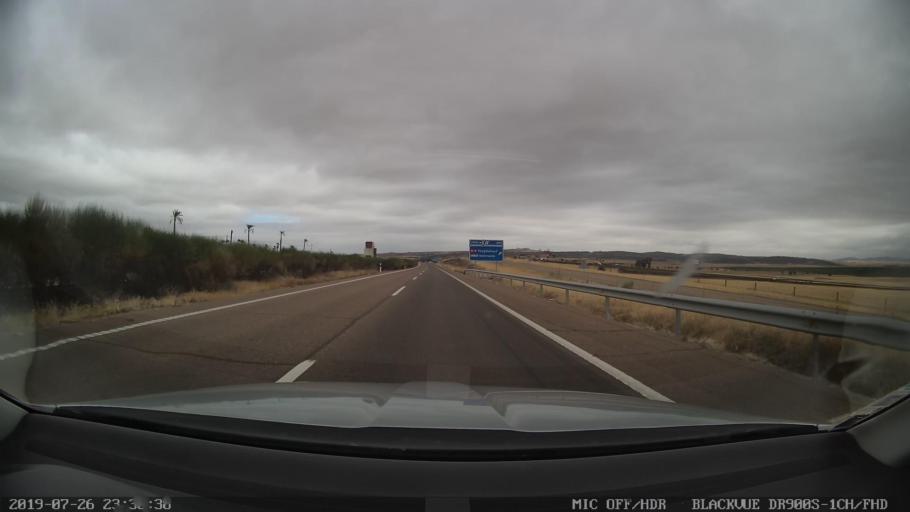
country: ES
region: Extremadura
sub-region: Provincia de Caceres
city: Trujillo
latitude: 39.3976
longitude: -5.8883
